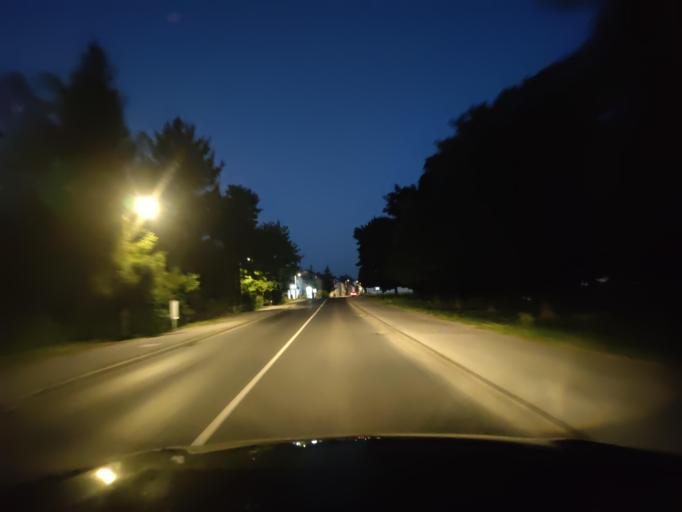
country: HR
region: Medimurska
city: Cakovec
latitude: 46.3834
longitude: 16.4464
